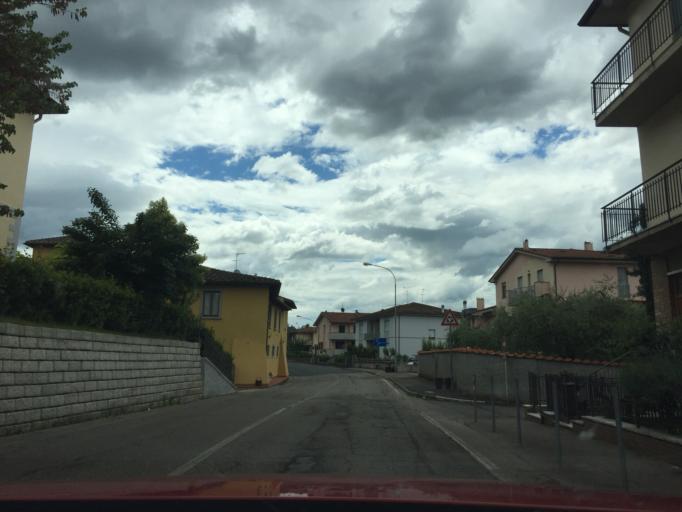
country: IT
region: Tuscany
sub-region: Province of Florence
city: Montelupo Fiorentino
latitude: 43.7295
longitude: 11.0258
